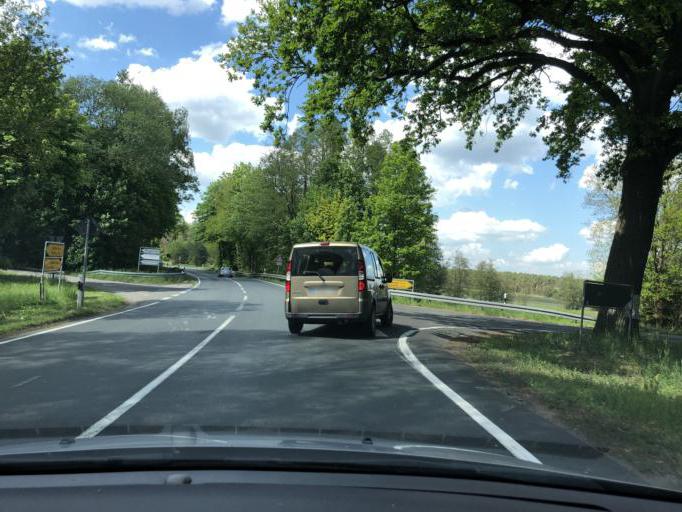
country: DE
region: Brandenburg
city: Spreenhagen
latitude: 52.3210
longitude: 13.9028
